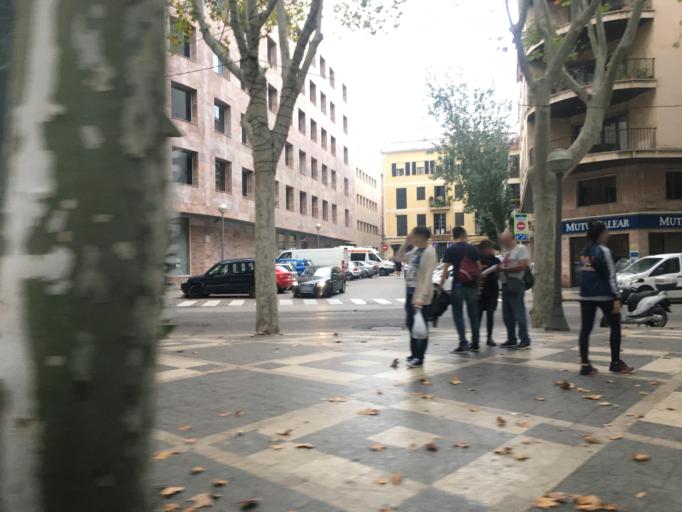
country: ES
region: Balearic Islands
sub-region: Illes Balears
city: Palma
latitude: 39.5739
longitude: 2.6492
